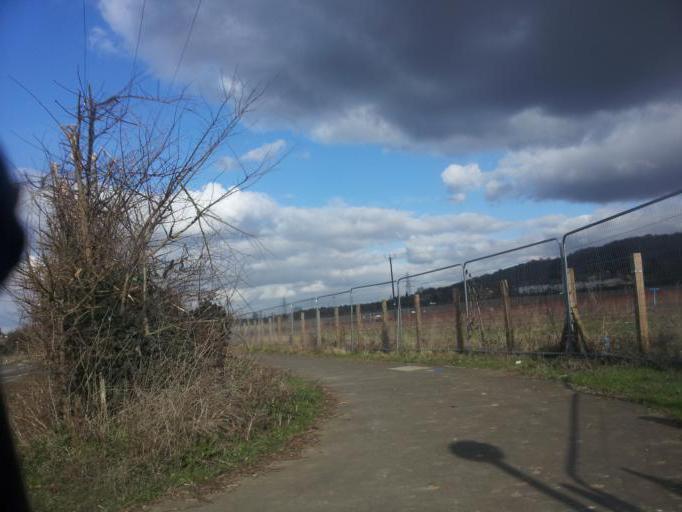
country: GB
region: England
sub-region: Medway
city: Halling
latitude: 51.3436
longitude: 0.4580
